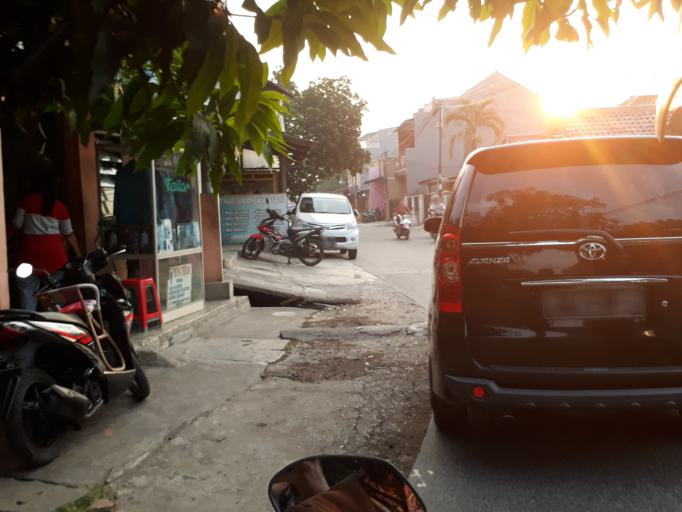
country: ID
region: West Java
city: Bekasi
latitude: -6.2395
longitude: 107.0362
